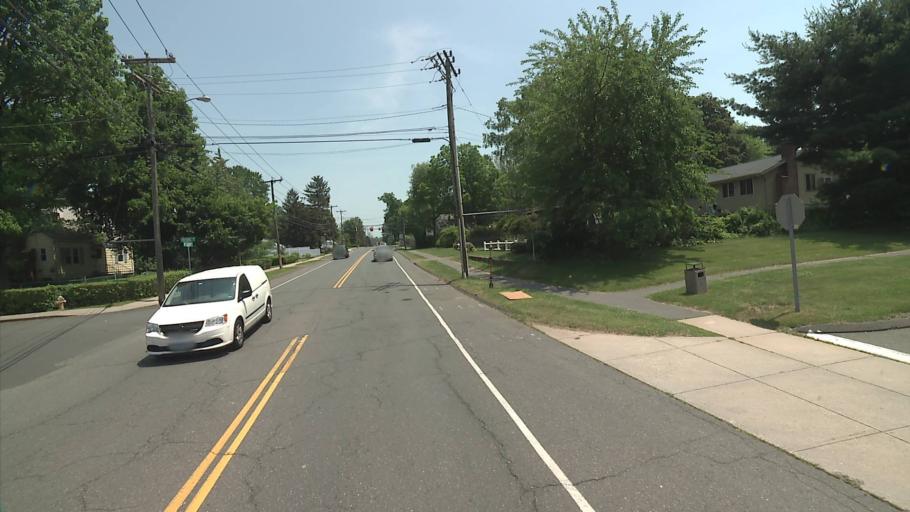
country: US
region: Connecticut
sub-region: Hartford County
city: Manchester
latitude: 41.7700
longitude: -72.5504
